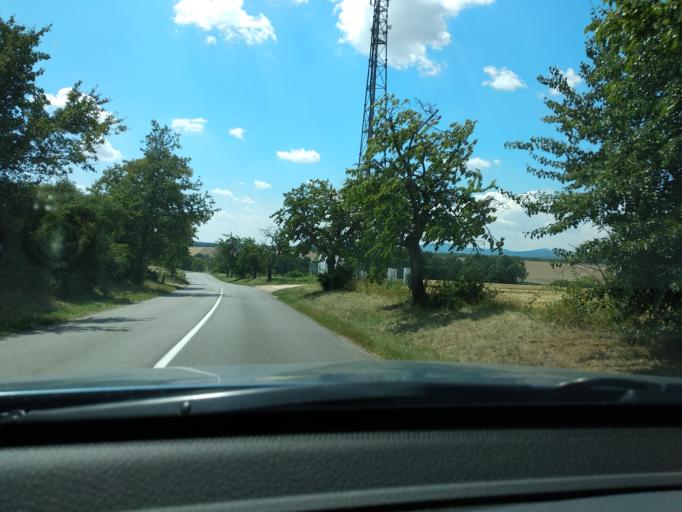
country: SK
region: Nitriansky
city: Banovce nad Bebravou
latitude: 48.6977
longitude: 18.2125
